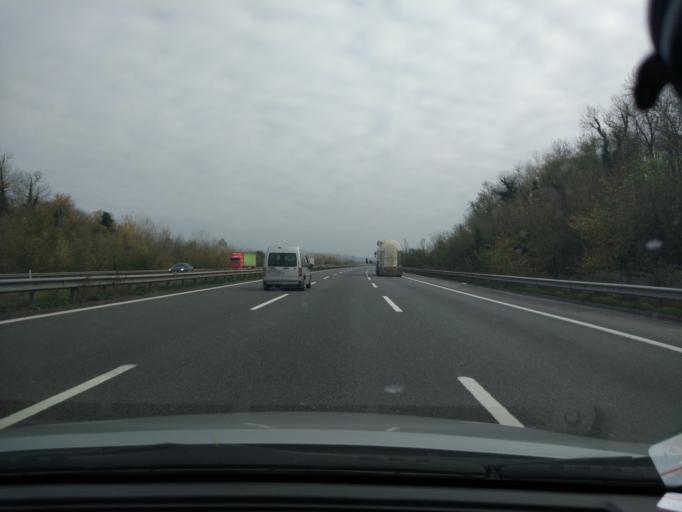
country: TR
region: Sakarya
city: Akyazi
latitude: 40.7387
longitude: 30.6483
